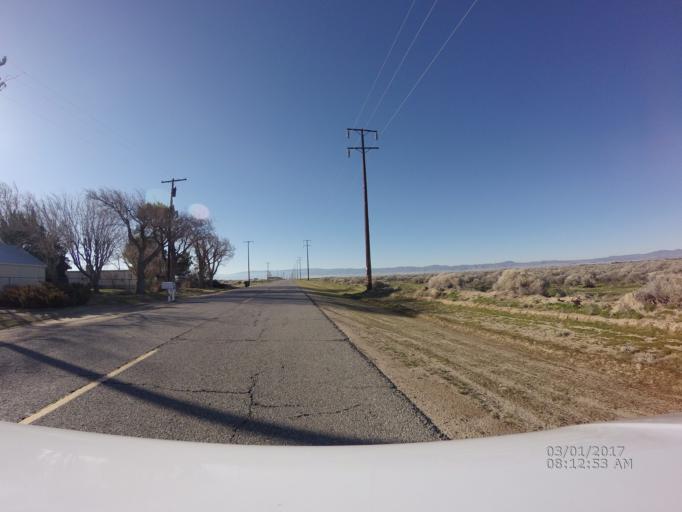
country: US
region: California
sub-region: Kern County
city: Rosamond
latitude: 34.7890
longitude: -118.2551
